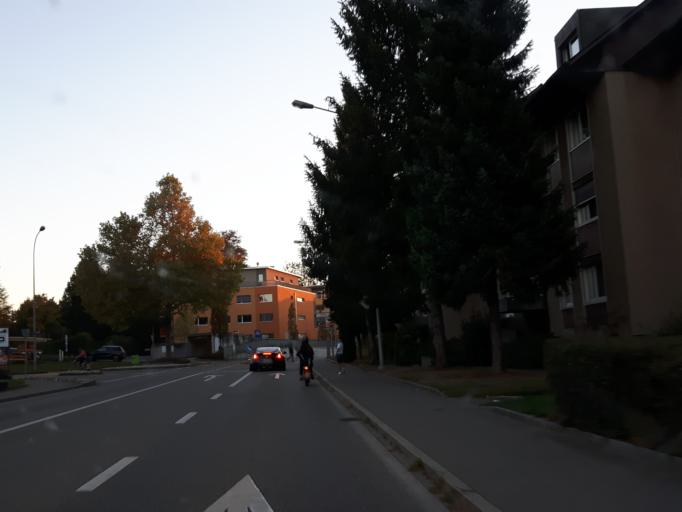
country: CH
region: Bern
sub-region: Oberaargau
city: Langenthal
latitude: 47.2142
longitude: 7.7938
